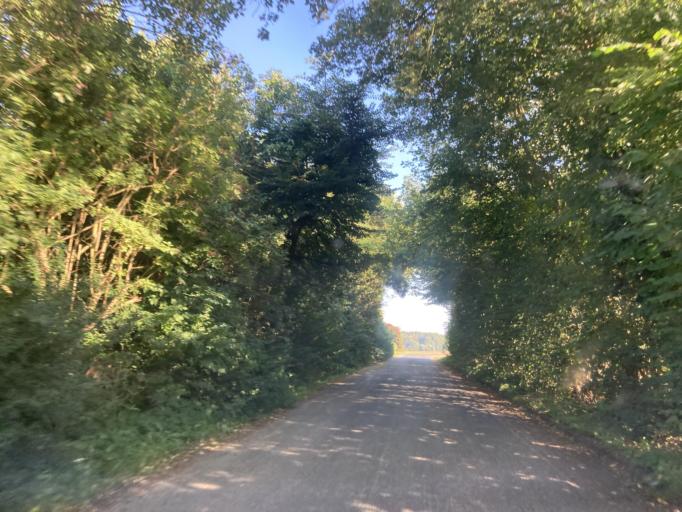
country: DK
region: South Denmark
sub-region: Svendborg Kommune
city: Thuro By
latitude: 55.1102
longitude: 10.7430
